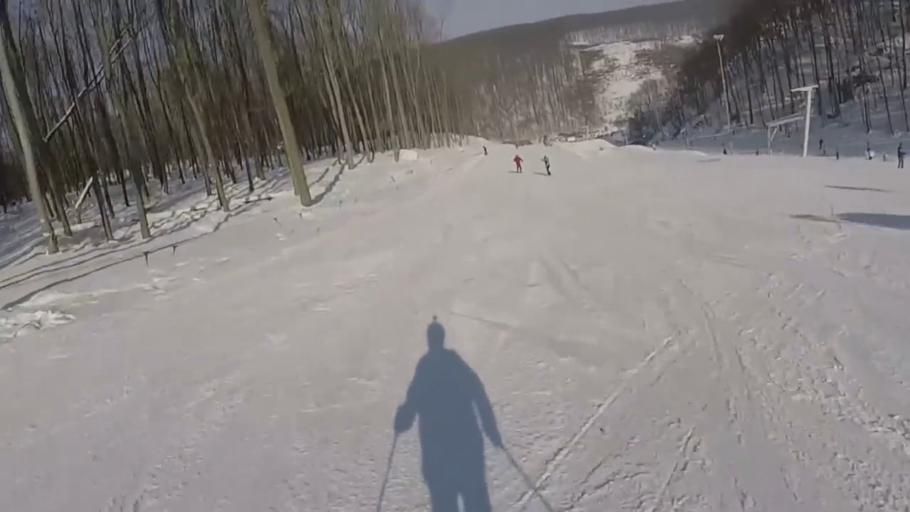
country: HU
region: Veszprem
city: Zirc
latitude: 47.2110
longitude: 17.9279
